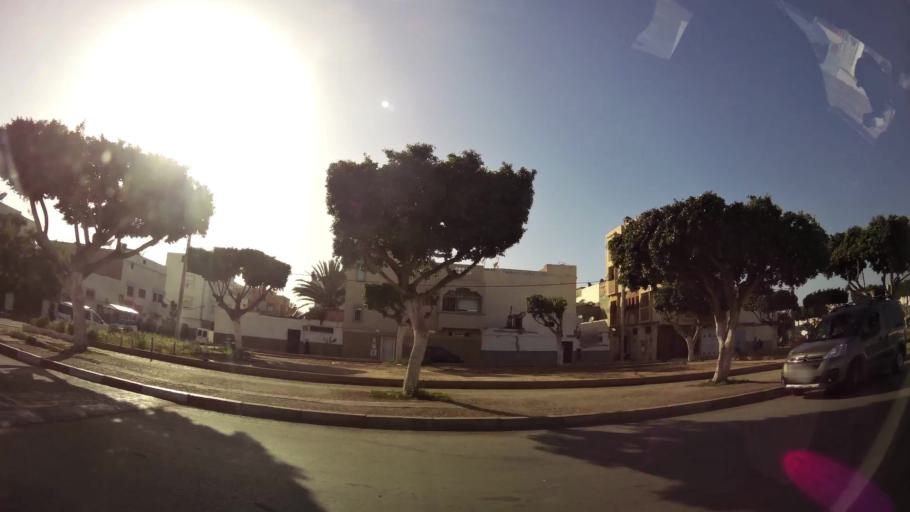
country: MA
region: Souss-Massa-Draa
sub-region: Agadir-Ida-ou-Tnan
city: Agadir
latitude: 30.4275
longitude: -9.5821
